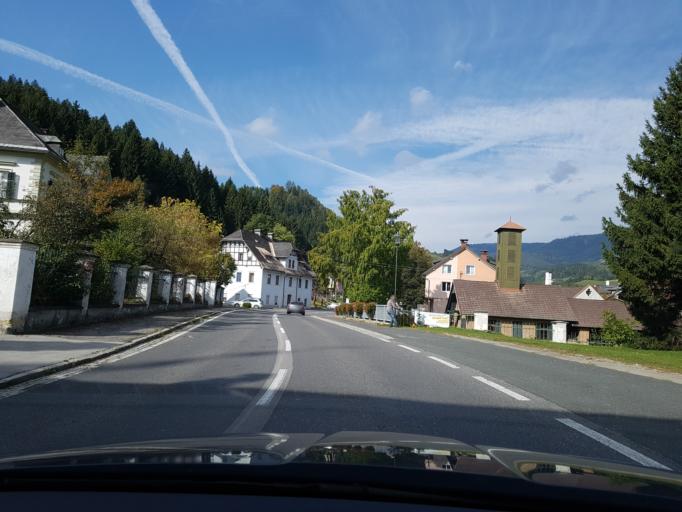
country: AT
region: Carinthia
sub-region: Politischer Bezirk Feldkirchen
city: Himmelberg
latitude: 46.7490
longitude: 14.0371
